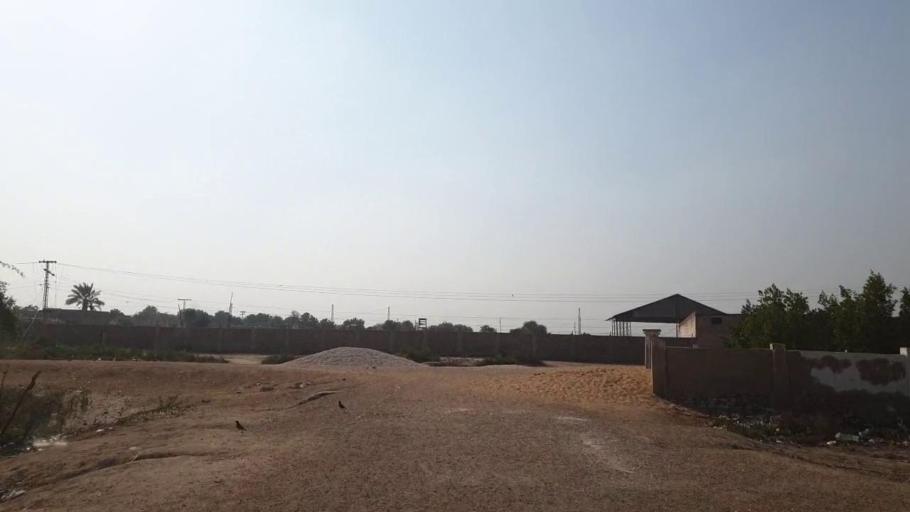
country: PK
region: Sindh
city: Mirpur Khas
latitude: 25.5013
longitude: 68.8837
